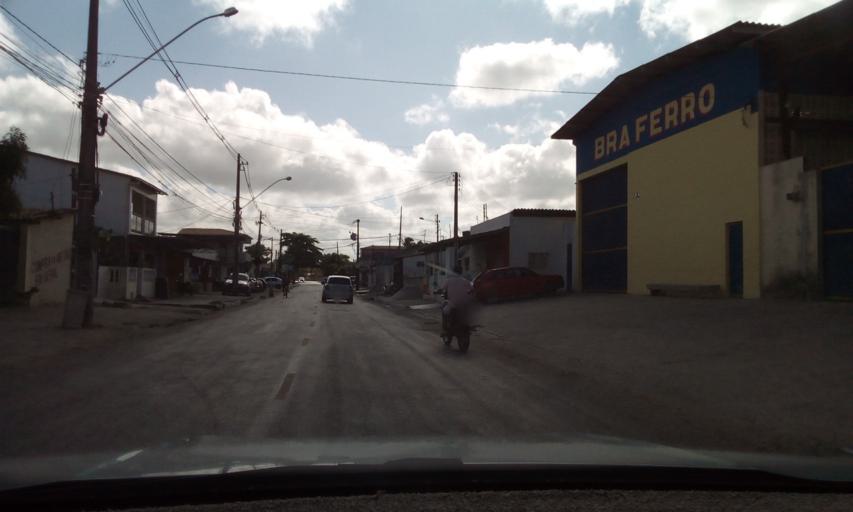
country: BR
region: Paraiba
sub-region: Bayeux
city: Bayeux
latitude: -7.1568
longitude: -34.9042
